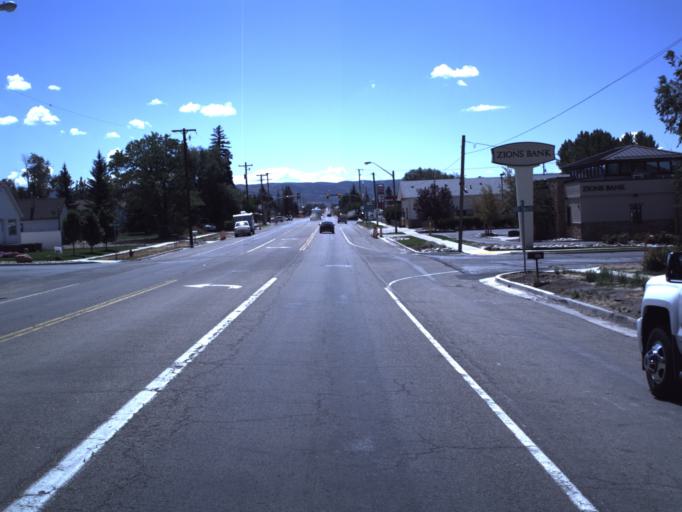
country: US
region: Utah
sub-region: Summit County
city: Kamas
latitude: 40.6419
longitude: -111.2808
